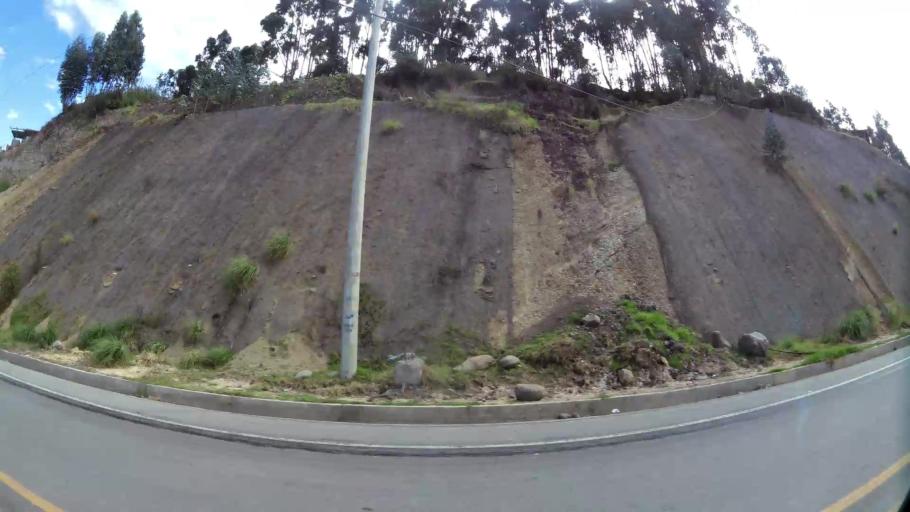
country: EC
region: Canar
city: Azogues
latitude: -2.7277
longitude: -78.8626
